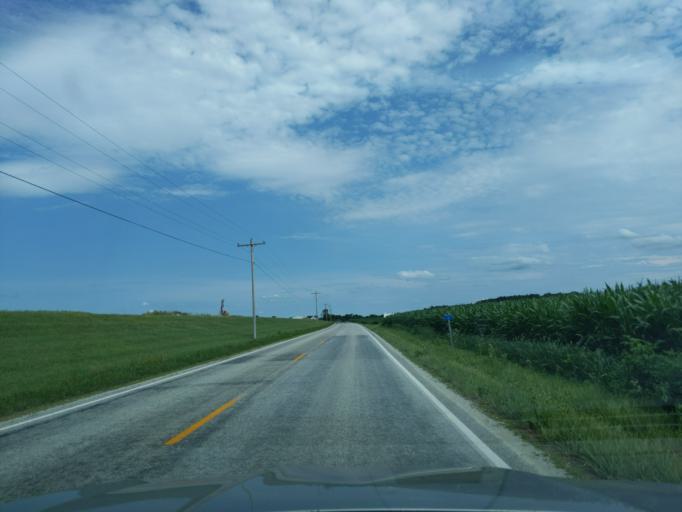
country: US
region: Indiana
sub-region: Ripley County
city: Osgood
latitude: 39.2021
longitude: -85.3130
